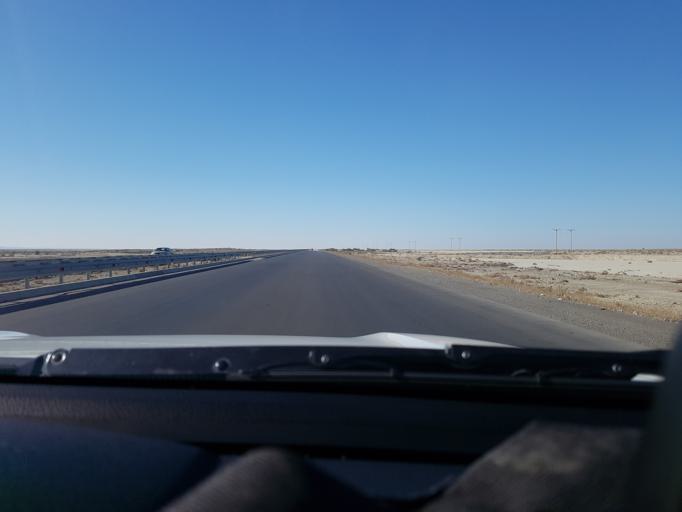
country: TM
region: Balkan
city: Gazanjyk
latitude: 39.2482
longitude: 55.0959
